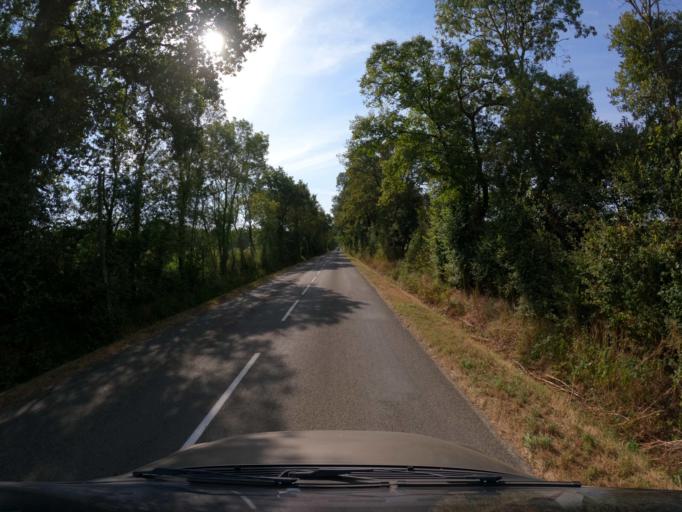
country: FR
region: Pays de la Loire
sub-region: Departement de la Vendee
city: Saint-Christophe-du-Ligneron
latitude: 46.8085
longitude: -1.8048
